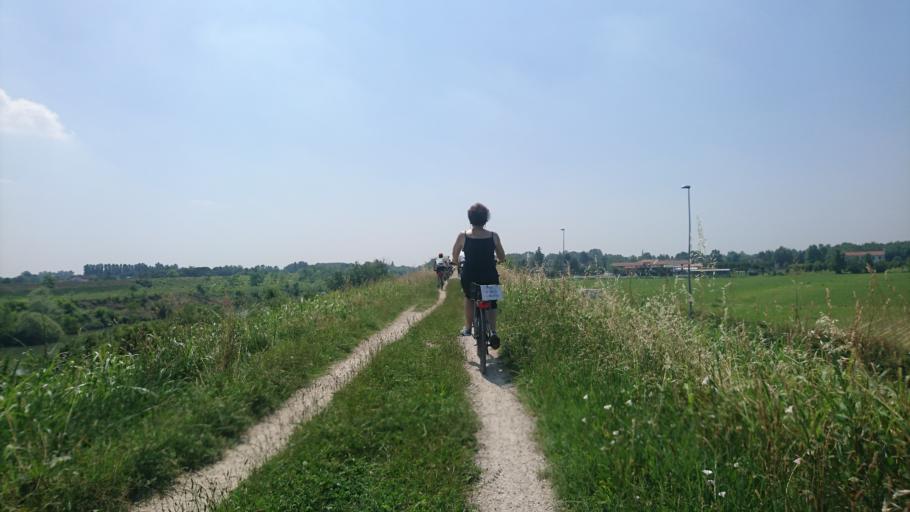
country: IT
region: Veneto
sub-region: Provincia di Padova
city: Oltre Brenta
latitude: 45.4031
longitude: 12.0010
